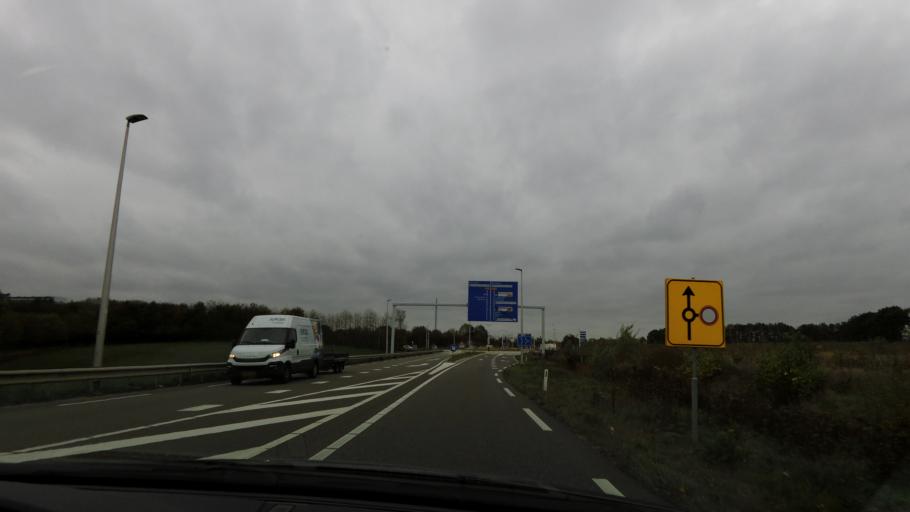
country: NL
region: Limburg
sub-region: Gemeente Onderbanken
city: Merkelbeek
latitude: 50.9473
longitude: 5.9476
